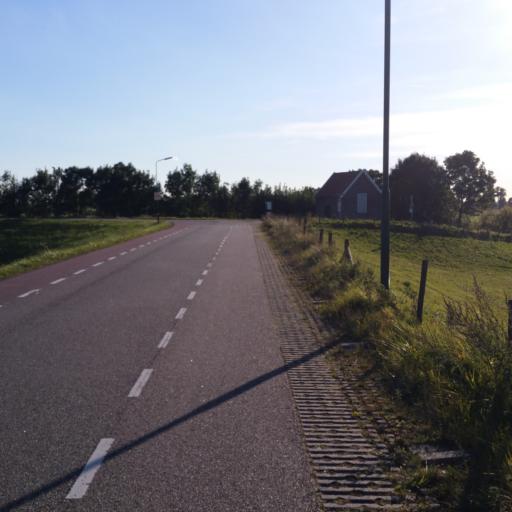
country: NL
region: Utrecht
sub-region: Gemeente Vianen
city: Vianen
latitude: 51.9975
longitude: 5.0643
